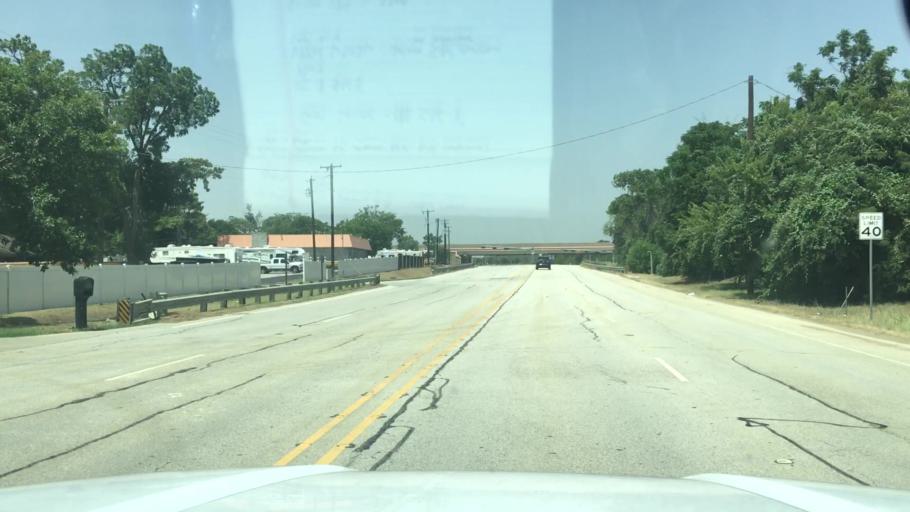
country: US
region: Texas
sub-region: Dallas County
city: Carrollton
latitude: 32.9686
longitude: -96.9289
